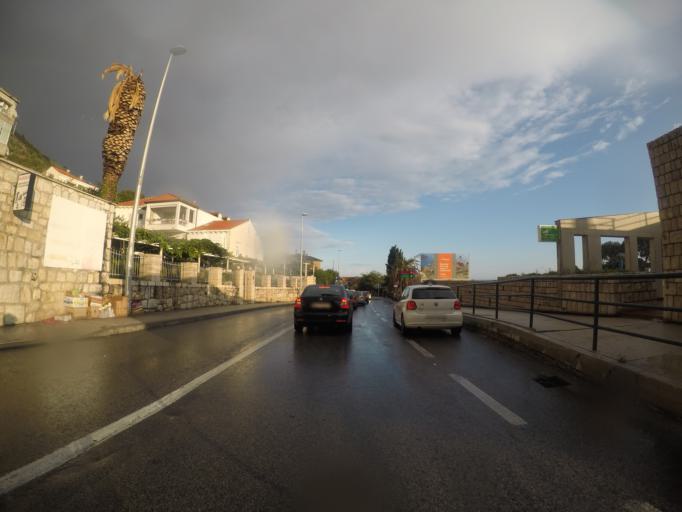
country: HR
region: Dubrovacko-Neretvanska
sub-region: Grad Dubrovnik
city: Dubrovnik
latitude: 42.6456
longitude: 18.1033
